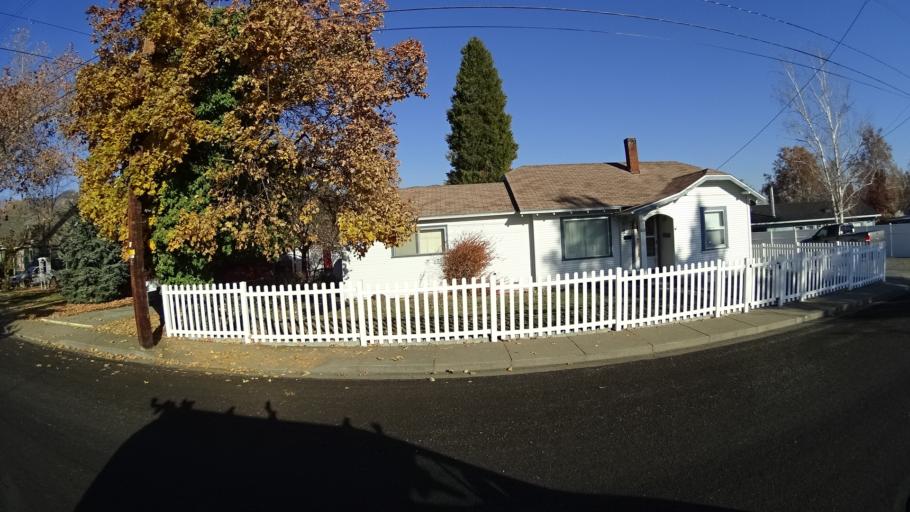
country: US
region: California
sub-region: Siskiyou County
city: Yreka
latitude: 41.7284
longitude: -122.6442
